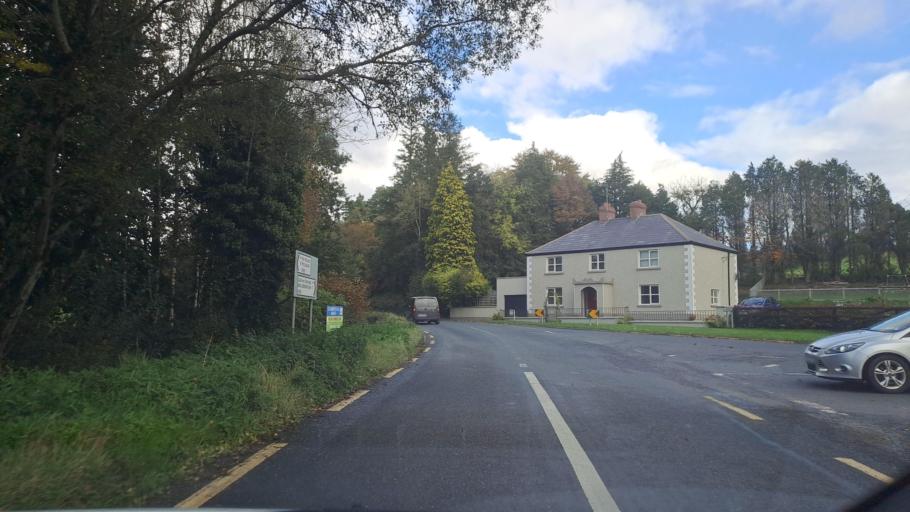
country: IE
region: Ulster
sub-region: An Cabhan
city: Mullagh
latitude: 53.8560
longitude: -6.9552
